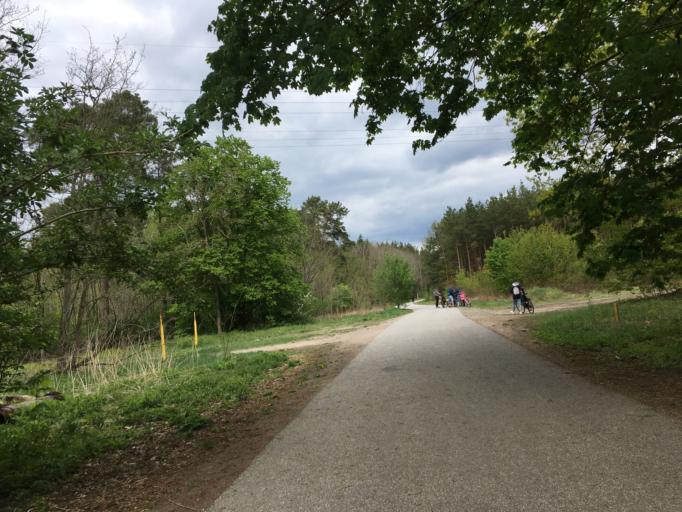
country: DE
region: Brandenburg
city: Bernau bei Berlin
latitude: 52.6831
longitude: 13.5329
